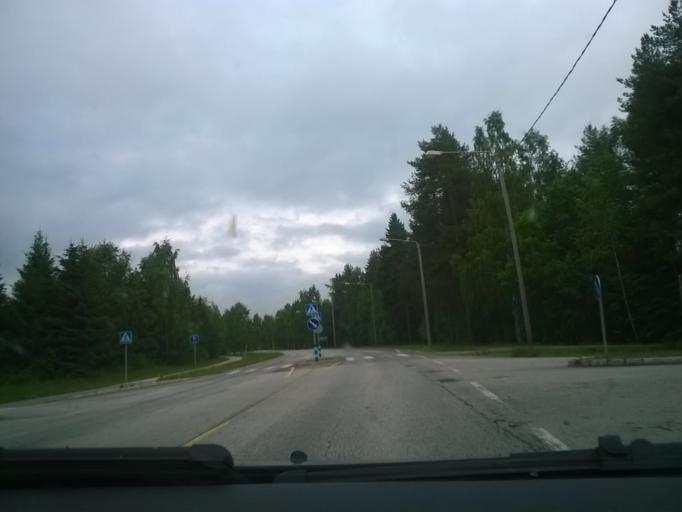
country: FI
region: Kainuu
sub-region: Kehys-Kainuu
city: Kuhmo
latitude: 64.1307
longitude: 29.4656
